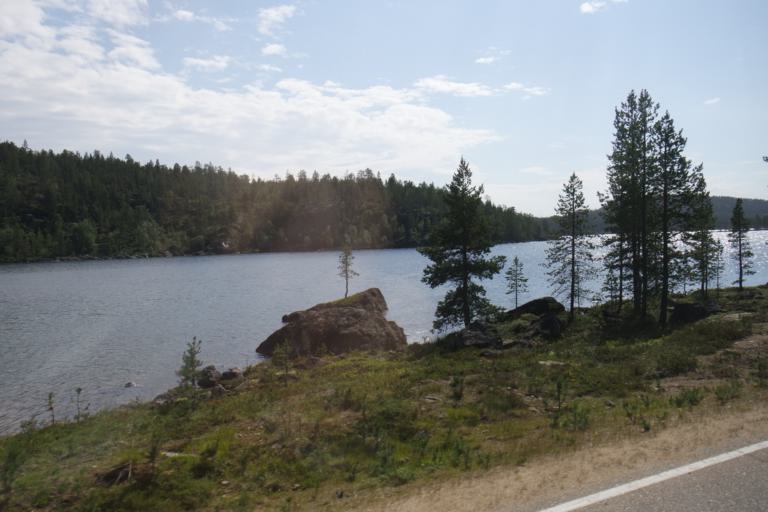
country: FI
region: Lapland
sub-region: Pohjois-Lappi
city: Ivalo
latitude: 68.8171
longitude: 27.3301
